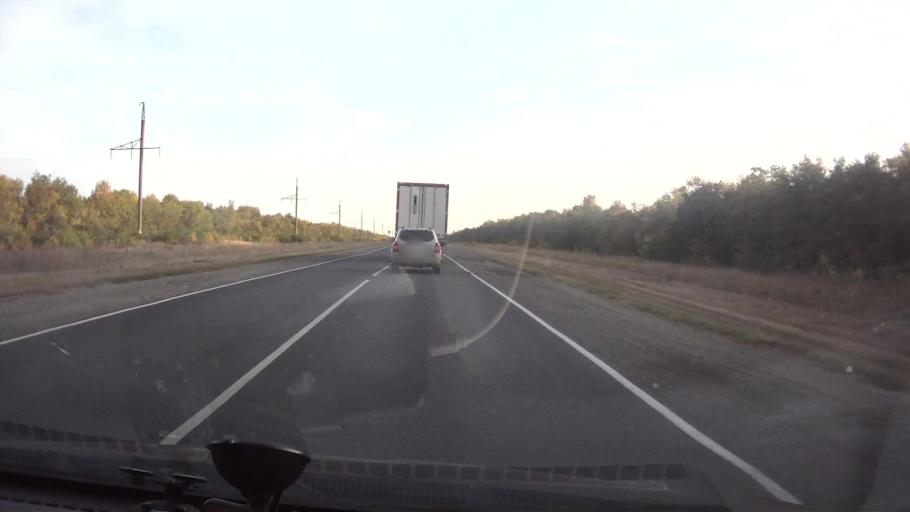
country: RU
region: Saratov
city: Krasnoarmeysk
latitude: 51.1274
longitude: 45.6505
